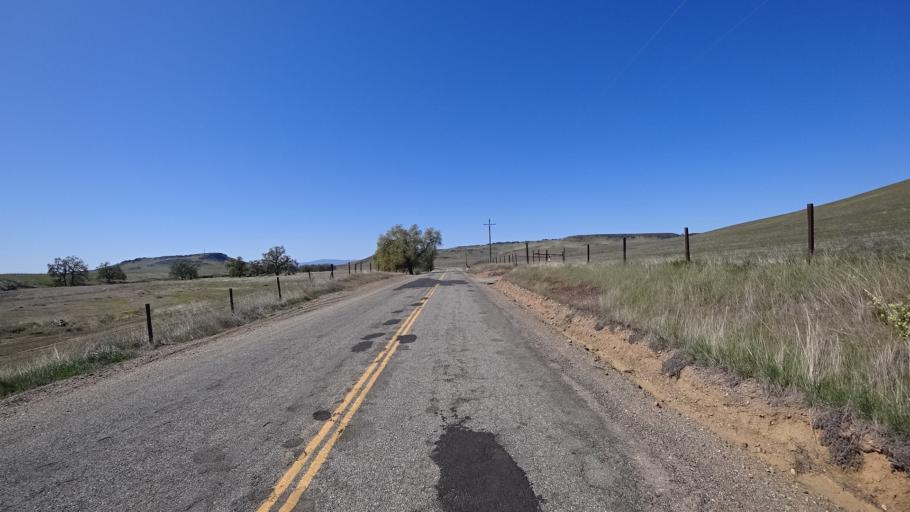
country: US
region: California
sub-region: Glenn County
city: Orland
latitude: 39.7783
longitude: -122.3119
